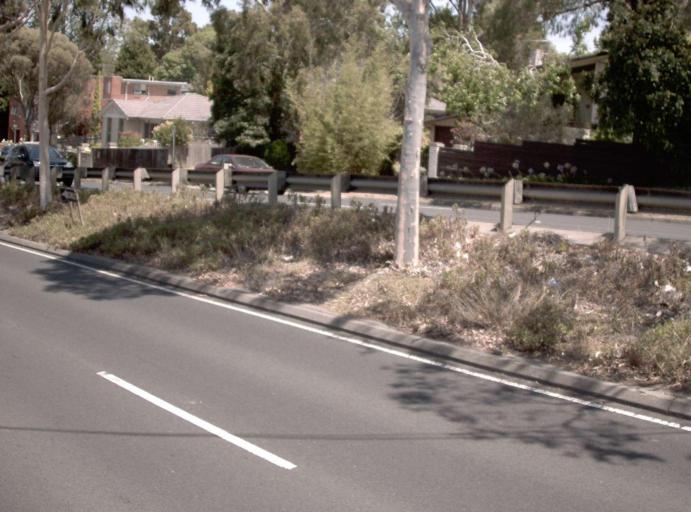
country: AU
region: Victoria
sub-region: Whitehorse
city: Vermont South
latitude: -37.8701
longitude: 145.1678
